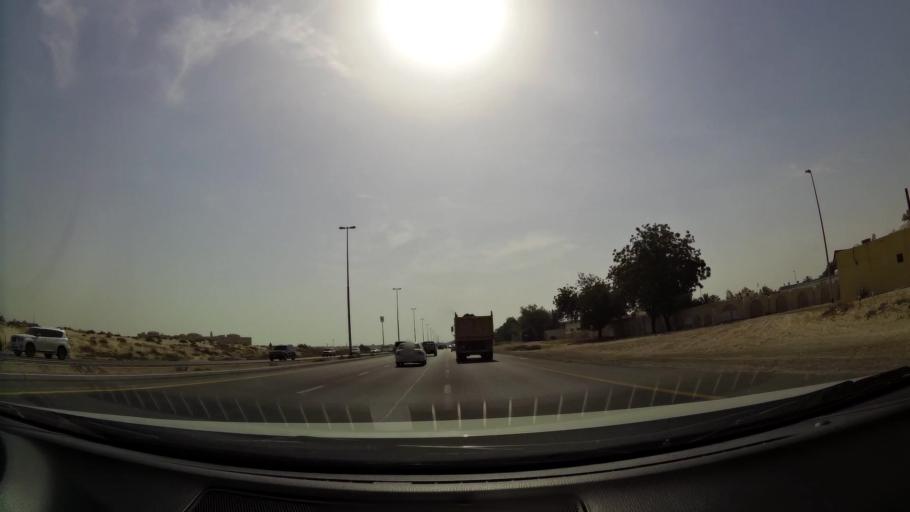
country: AE
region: Ash Shariqah
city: Sharjah
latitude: 25.2536
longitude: 55.4206
